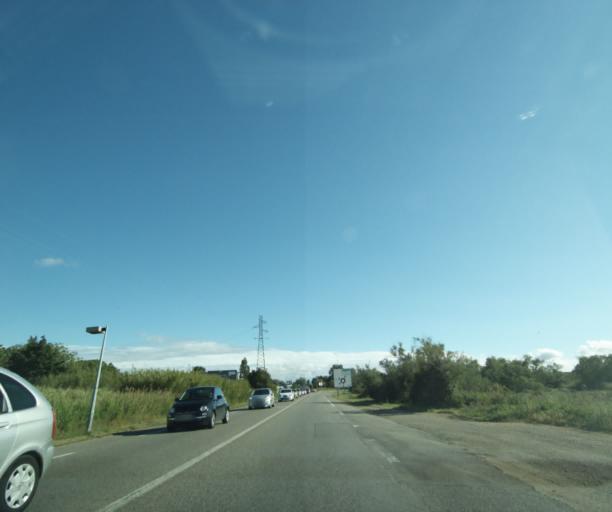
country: FR
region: Provence-Alpes-Cote d'Azur
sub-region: Departement des Bouches-du-Rhone
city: Vitrolles
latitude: 43.4504
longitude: 5.2308
